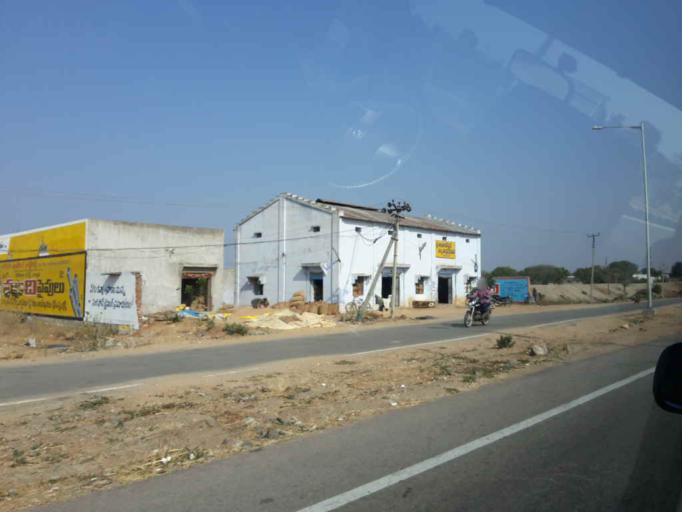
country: IN
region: Telangana
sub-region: Nizamabad District
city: Nizamabad
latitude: 18.5417
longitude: 78.2411
